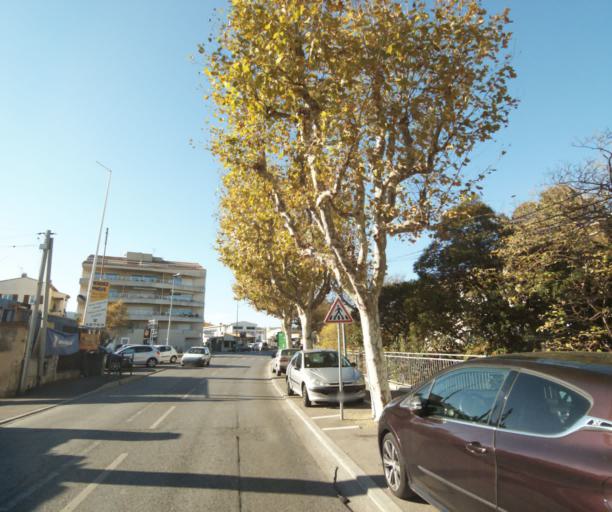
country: FR
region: Provence-Alpes-Cote d'Azur
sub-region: Departement des Bouches-du-Rhone
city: La Ciotat
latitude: 43.1834
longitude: 5.6109
